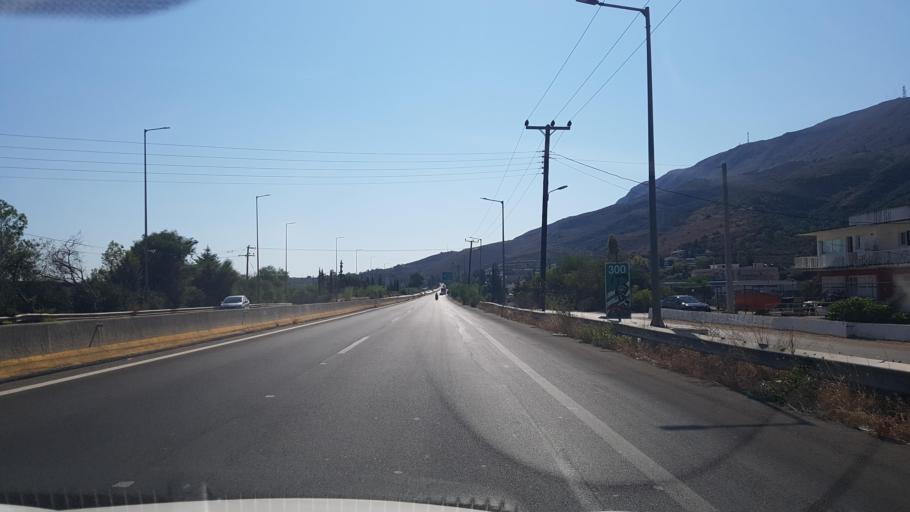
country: GR
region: Crete
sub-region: Nomos Chanias
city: Tsikalaria
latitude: 35.4807
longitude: 24.0589
